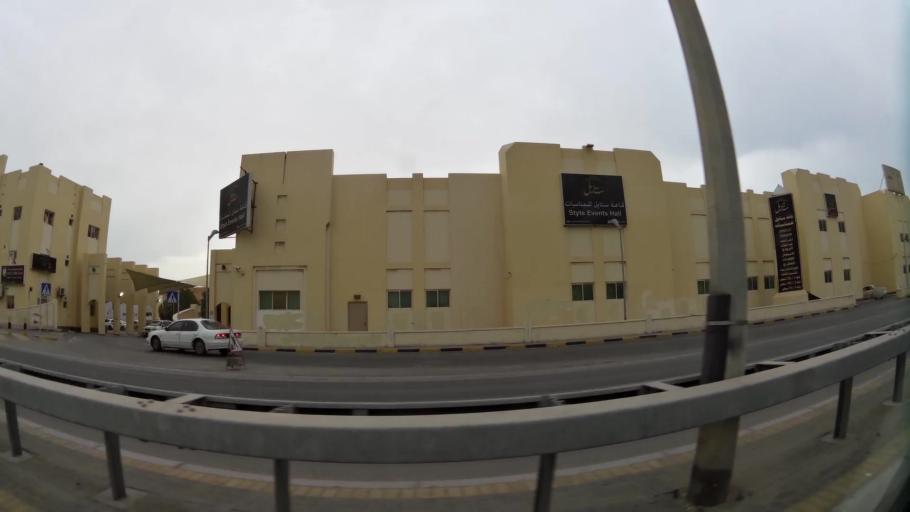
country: BH
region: Central Governorate
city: Madinat Hamad
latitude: 26.0942
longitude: 50.4887
